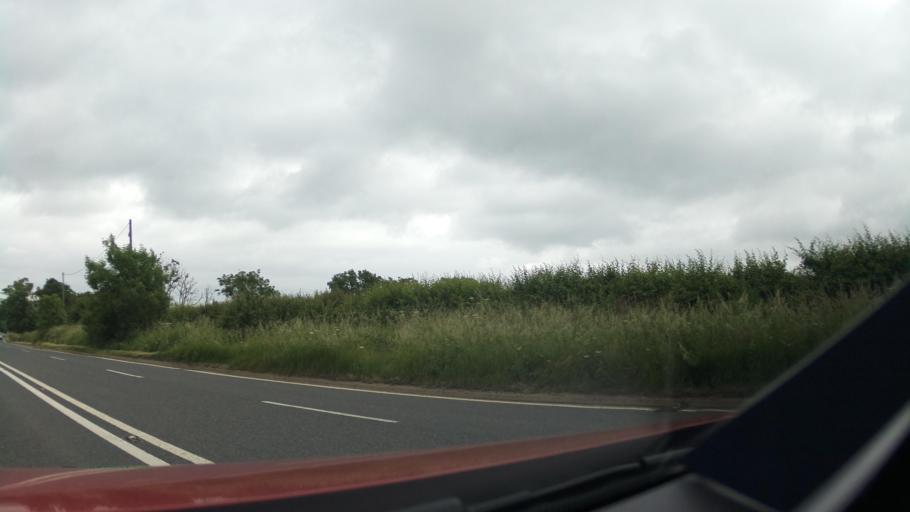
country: GB
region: England
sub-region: District of Rutland
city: Ridlington
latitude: 52.5943
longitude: -0.8335
